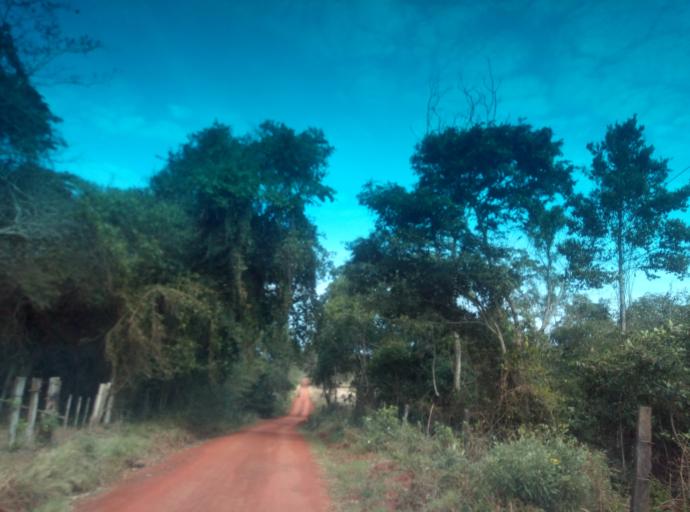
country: PY
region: Caaguazu
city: Carayao
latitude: -25.2004
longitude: -56.2528
